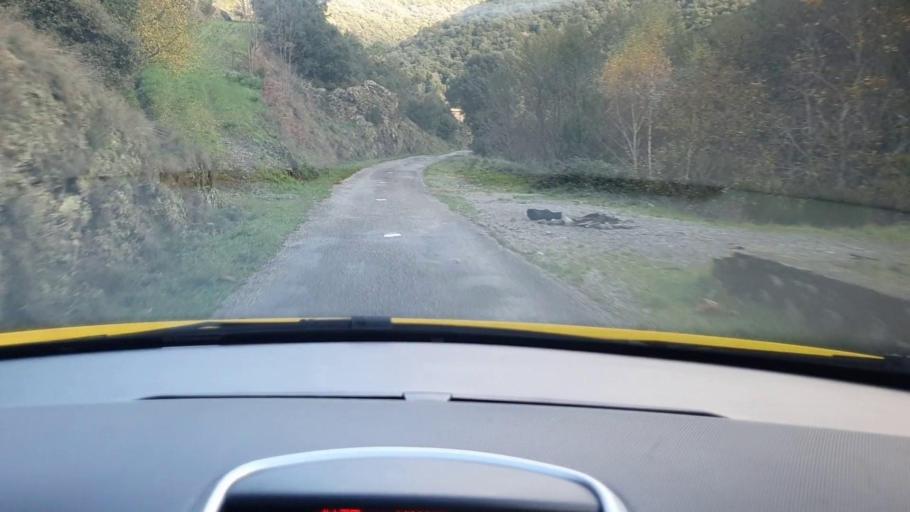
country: FR
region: Languedoc-Roussillon
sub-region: Departement du Gard
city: Valleraugue
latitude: 44.0988
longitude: 3.7345
